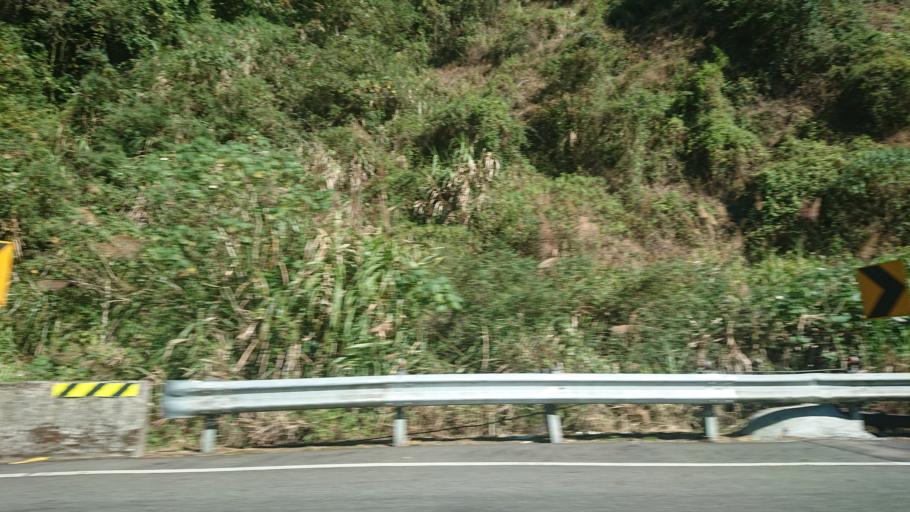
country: TW
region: Taiwan
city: Lugu
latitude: 23.4921
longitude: 120.7580
